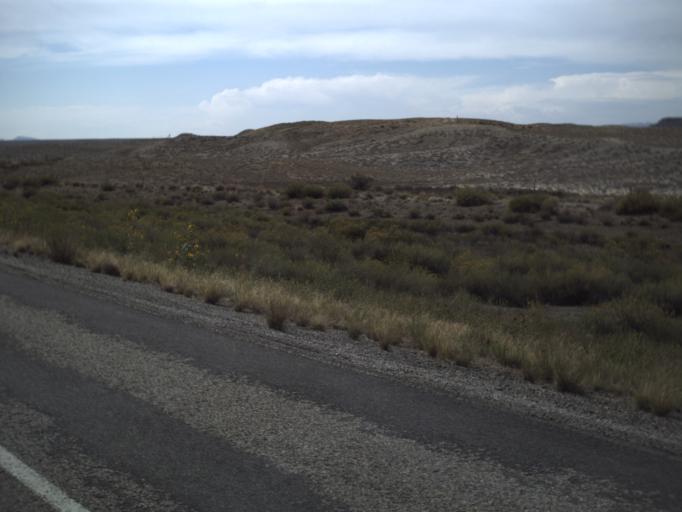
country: US
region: Utah
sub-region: Grand County
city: Moab
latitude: 38.9370
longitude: -109.4116
